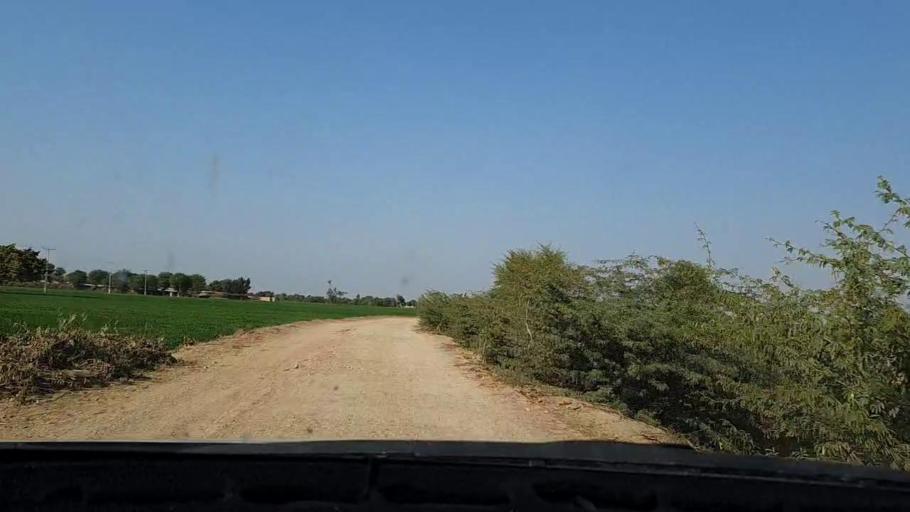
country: PK
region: Sindh
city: Tando Mittha Khan
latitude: 25.8129
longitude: 69.3147
